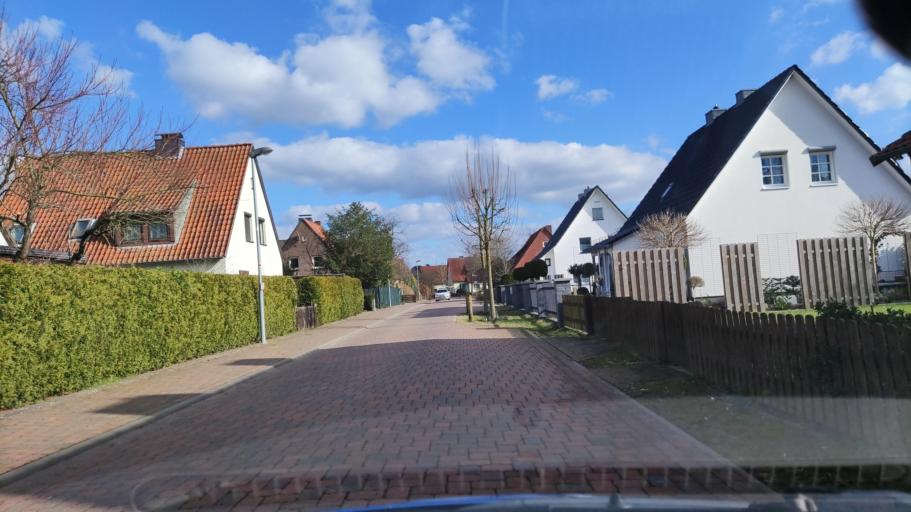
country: DE
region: Lower Saxony
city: Eldingen
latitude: 52.6835
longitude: 10.3428
